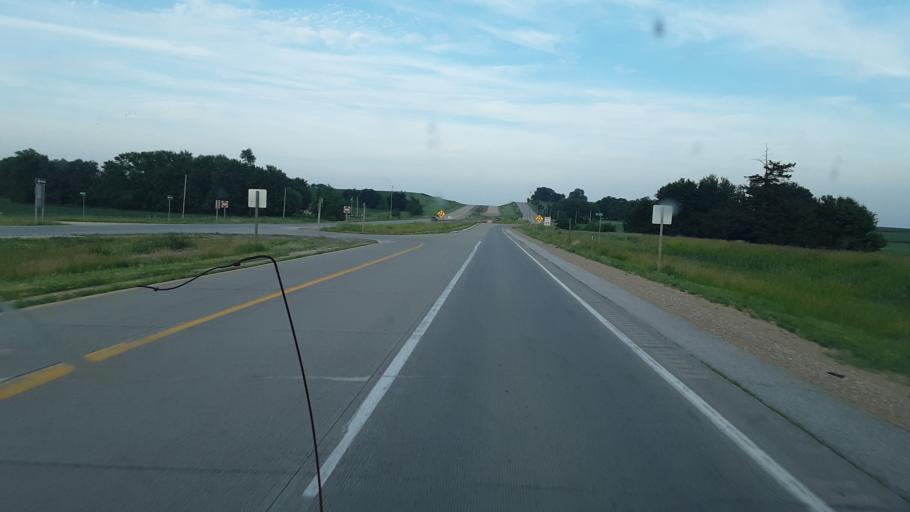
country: US
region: Iowa
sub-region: Tama County
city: Tama
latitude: 41.9642
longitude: -92.5341
